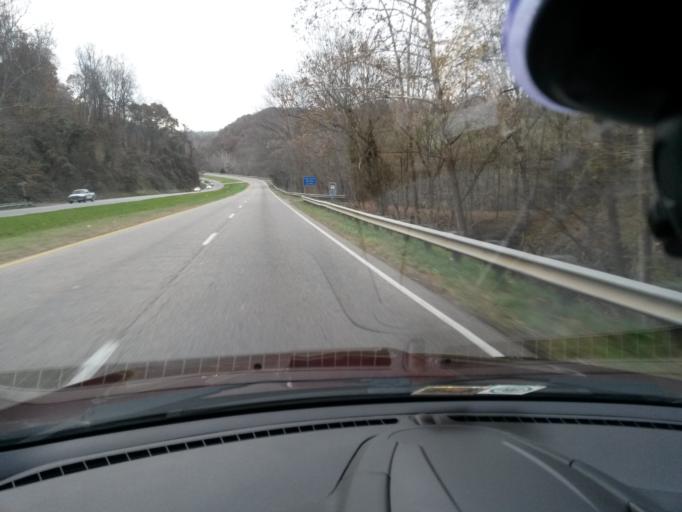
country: US
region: Virginia
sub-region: City of Buena Vista
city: Buena Vista
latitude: 37.7453
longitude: -79.3839
